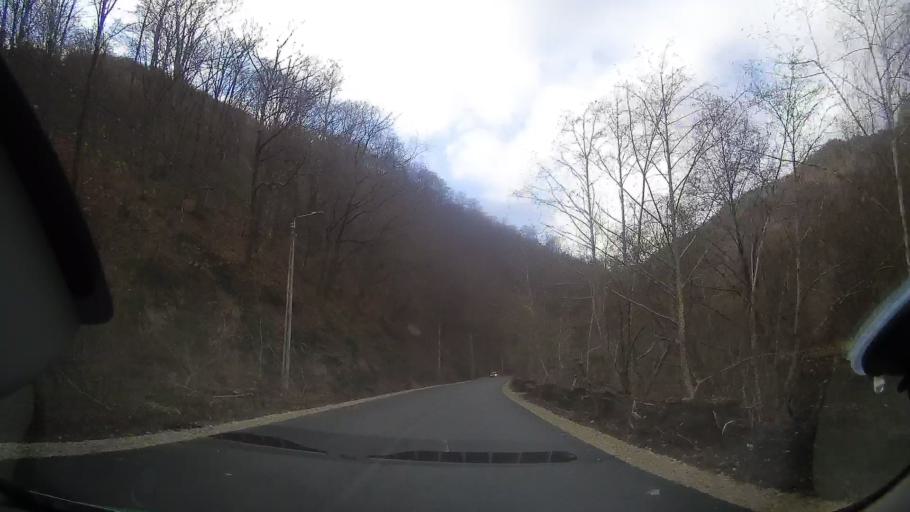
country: RO
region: Cluj
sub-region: Comuna Valea Ierii
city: Valea Ierii
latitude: 46.6907
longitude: 23.3053
